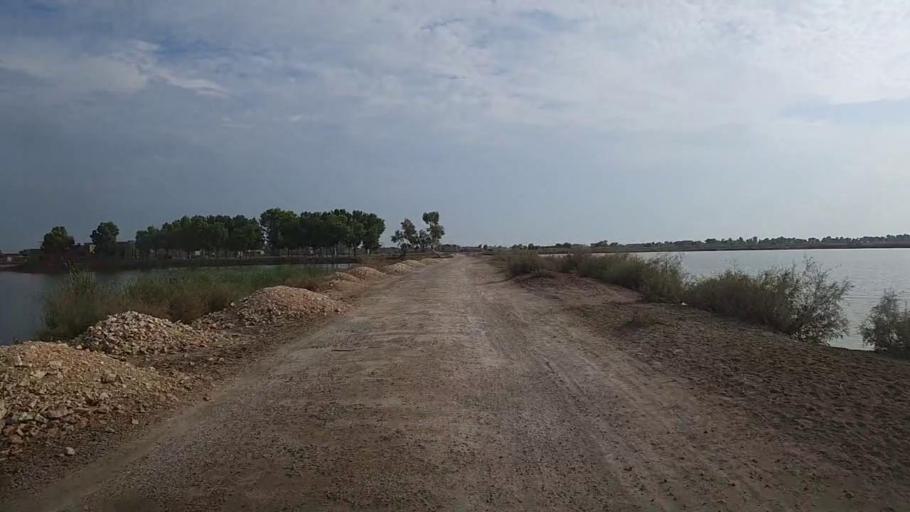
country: PK
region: Sindh
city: Thul
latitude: 28.2725
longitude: 68.8541
